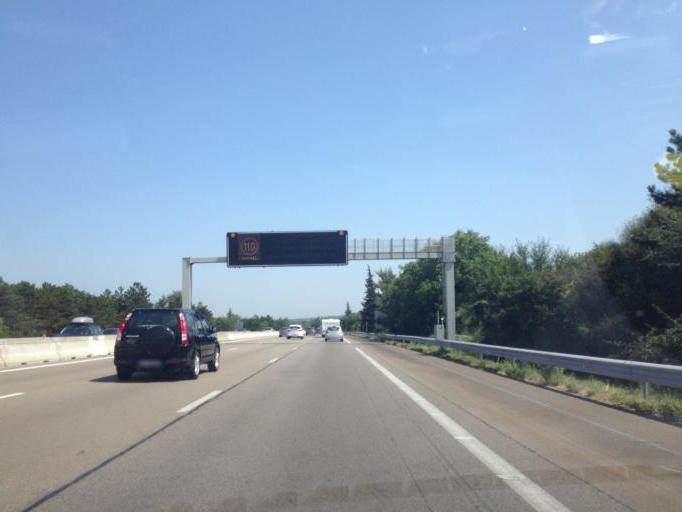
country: FR
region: Rhone-Alpes
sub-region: Departement de l'Ardeche
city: Cruas
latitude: 44.6508
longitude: 4.7939
